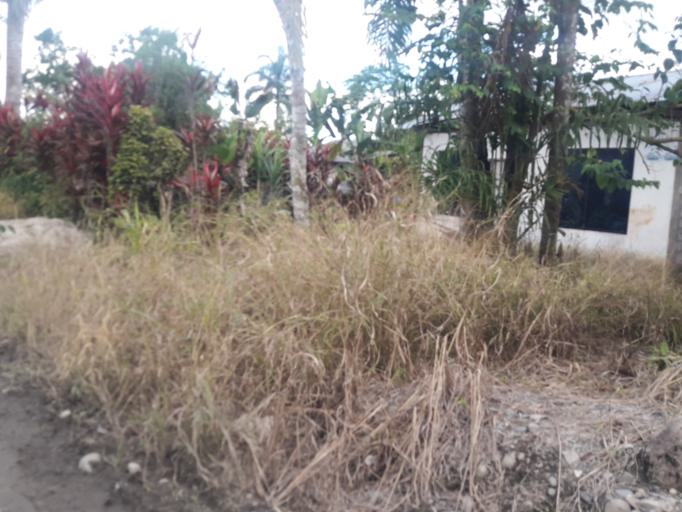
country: EC
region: Napo
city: Tena
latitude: -0.9714
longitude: -77.8397
